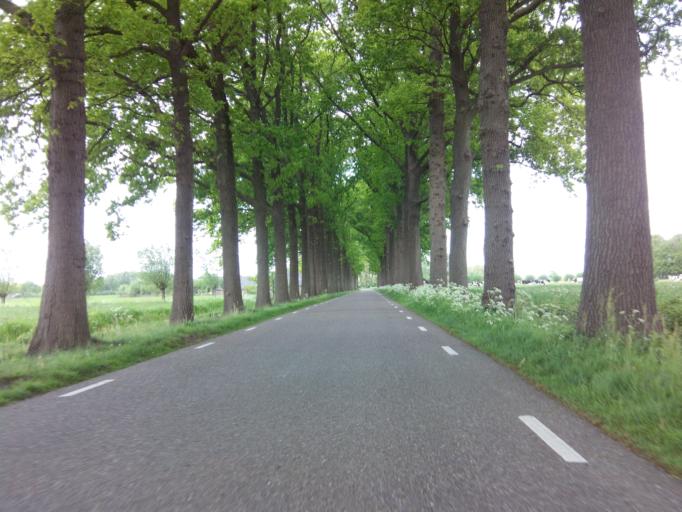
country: NL
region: Utrecht
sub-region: Gemeente Utrechtse Heuvelrug
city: Overberg
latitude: 52.0713
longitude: 5.4702
